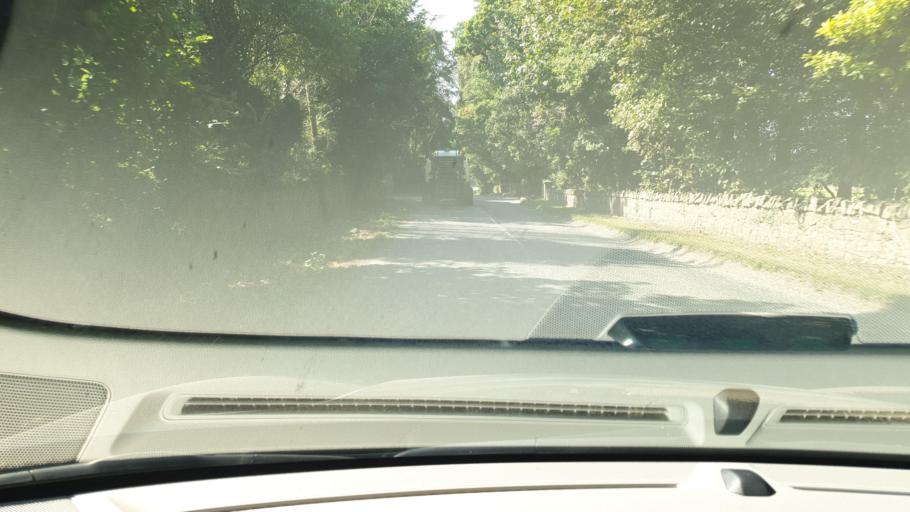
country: IE
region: Leinster
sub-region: An Mhi
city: Athboy
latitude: 53.5985
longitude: -6.8728
